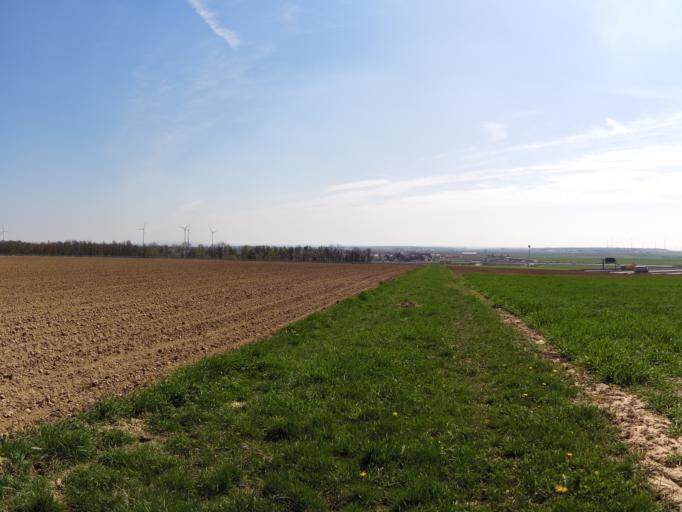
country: DE
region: Bavaria
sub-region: Regierungsbezirk Unterfranken
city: Biebelried
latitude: 49.7752
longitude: 10.0759
